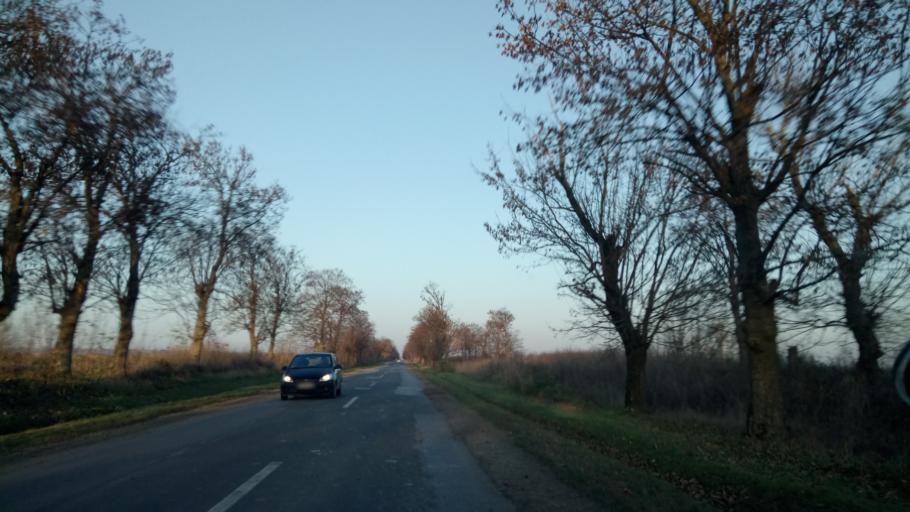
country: RS
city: Novi Slankamen
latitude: 45.1058
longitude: 20.2128
